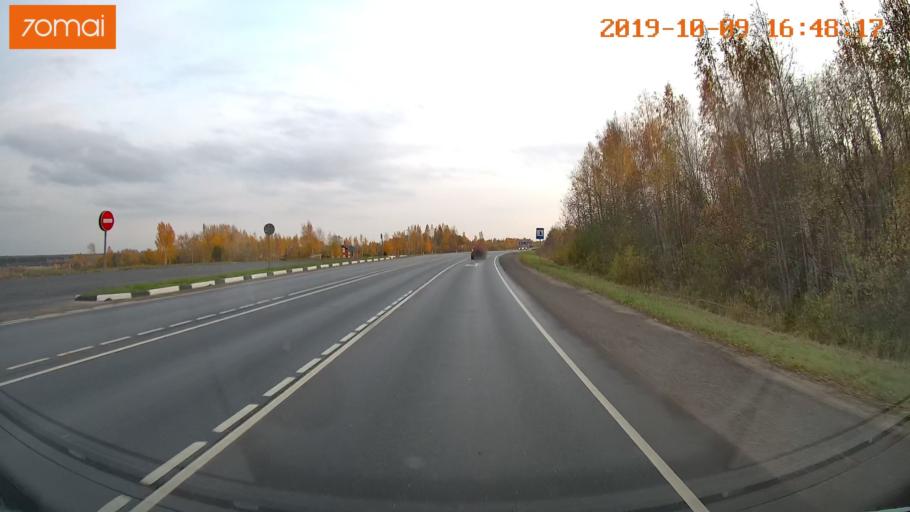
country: RU
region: Kostroma
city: Volgorechensk
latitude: 57.4290
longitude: 41.1899
